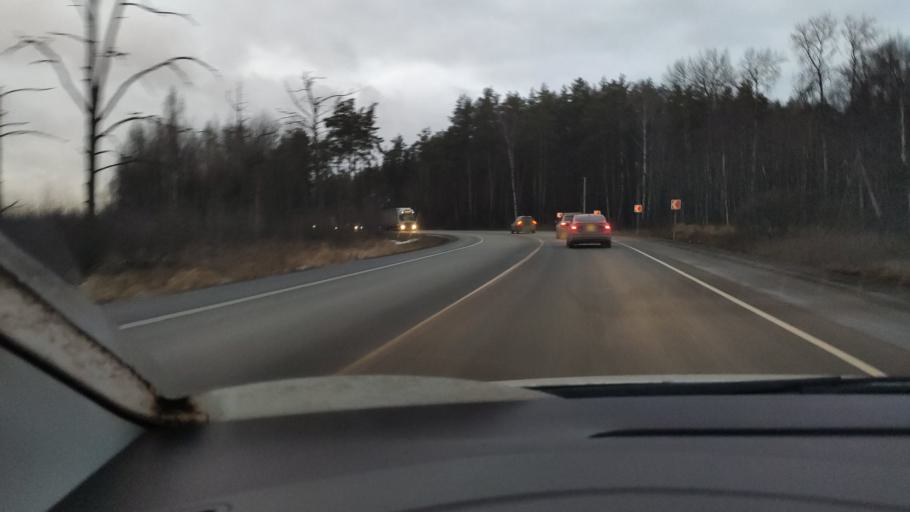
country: RU
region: Moskovskaya
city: Fryazevo
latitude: 55.7477
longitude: 38.4530
